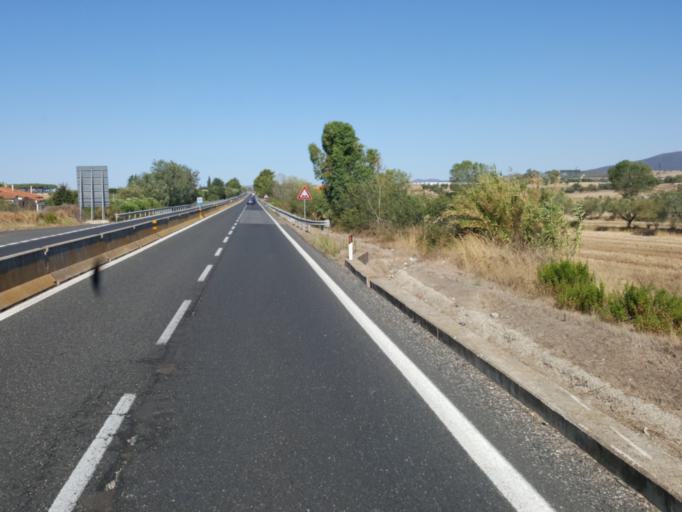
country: IT
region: Latium
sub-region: Provincia di Viterbo
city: Pescia Romana
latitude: 42.4033
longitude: 11.4963
